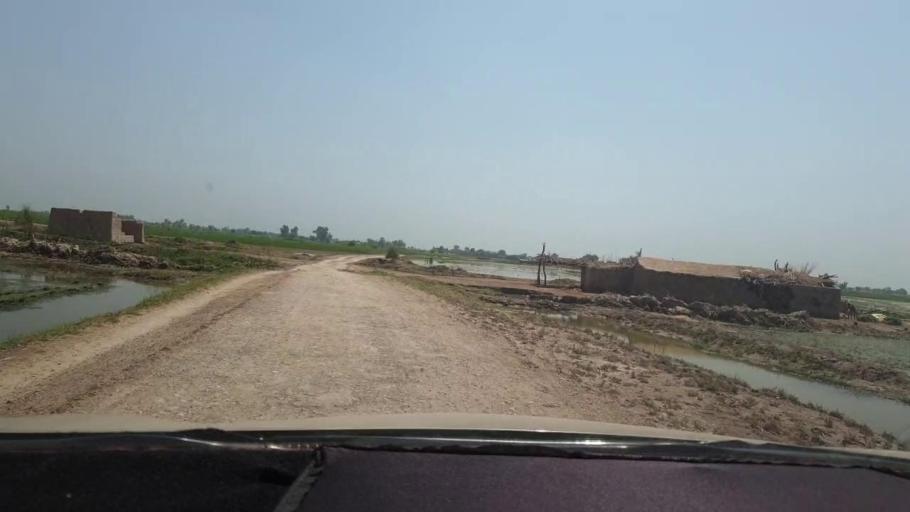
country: PK
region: Sindh
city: Shahdadkot
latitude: 27.8227
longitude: 67.9961
